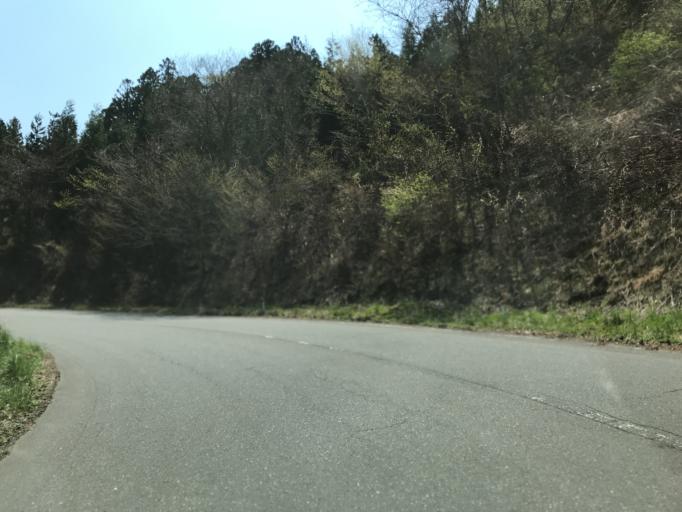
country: JP
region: Ibaraki
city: Kitaibaraki
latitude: 36.9784
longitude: 140.6258
